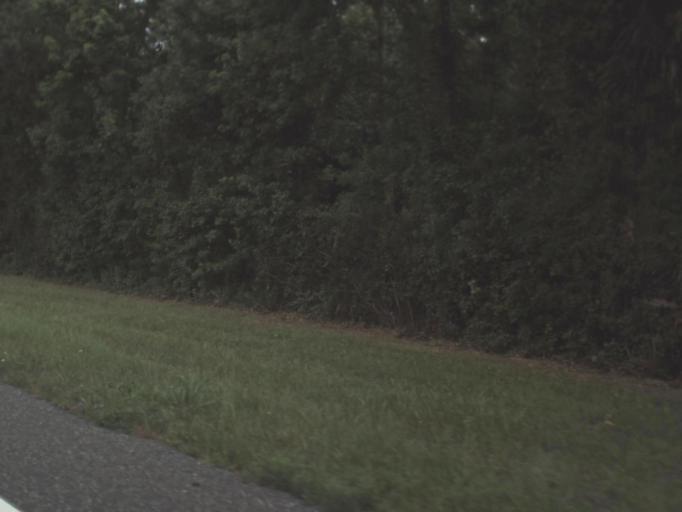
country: US
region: Florida
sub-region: Levy County
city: Bronson
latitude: 29.2782
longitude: -82.7389
